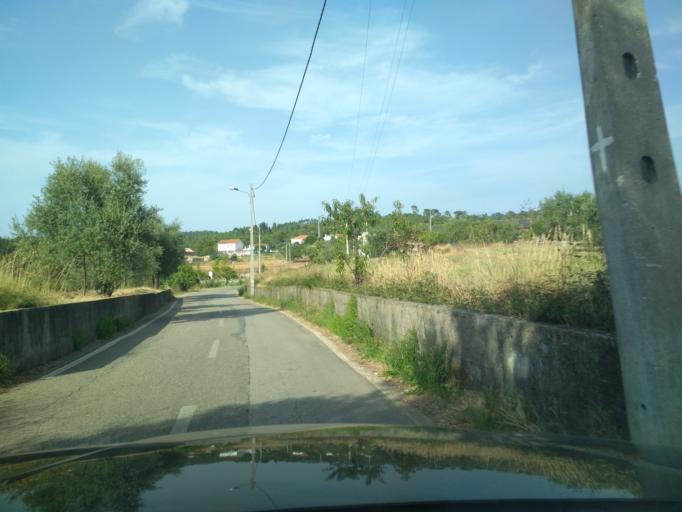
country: PT
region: Coimbra
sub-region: Condeixa-A-Nova
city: Condeixa-a-Nova
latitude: 40.1364
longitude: -8.4572
